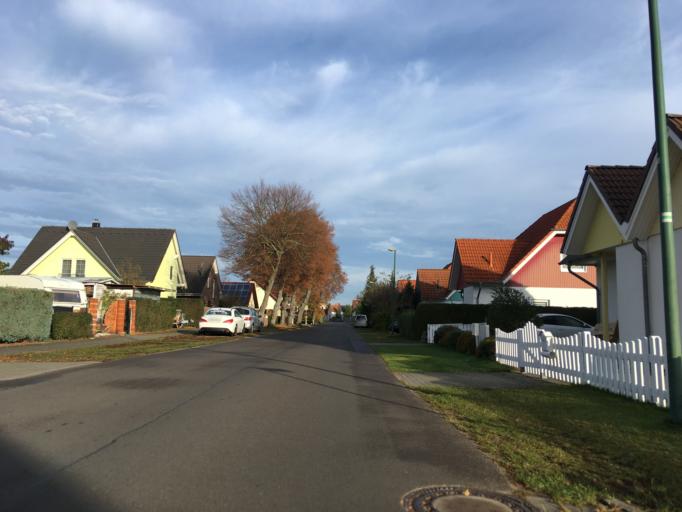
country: DE
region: Brandenburg
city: Luebben
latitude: 51.9667
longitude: 13.8857
